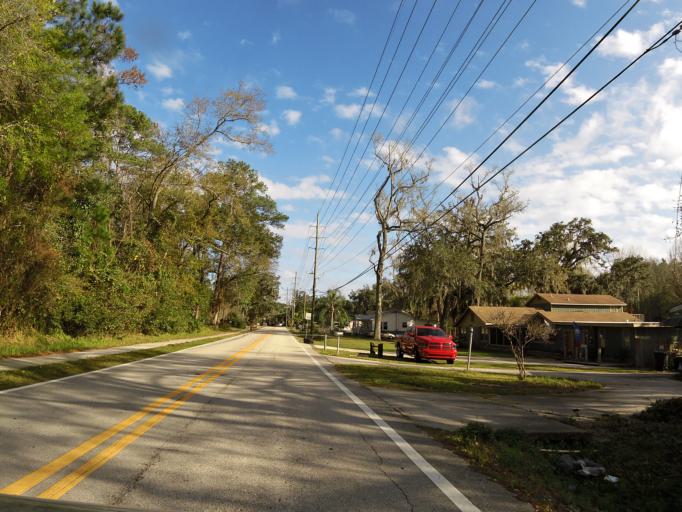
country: US
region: Florida
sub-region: Duval County
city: Jacksonville
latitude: 30.2874
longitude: -81.6185
